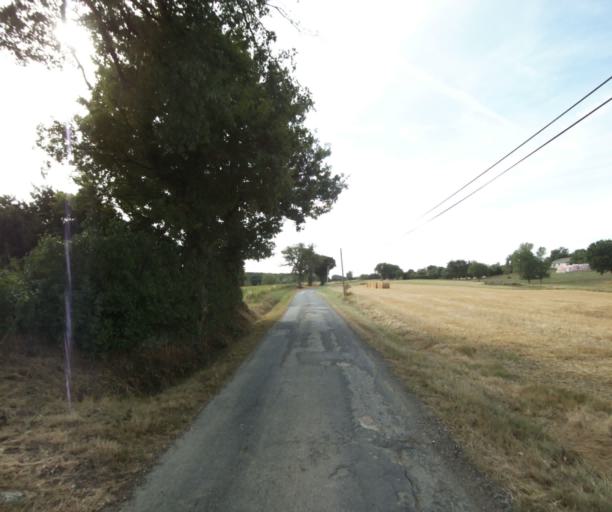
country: FR
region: Midi-Pyrenees
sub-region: Departement du Tarn
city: Puylaurens
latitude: 43.5311
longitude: 2.0571
